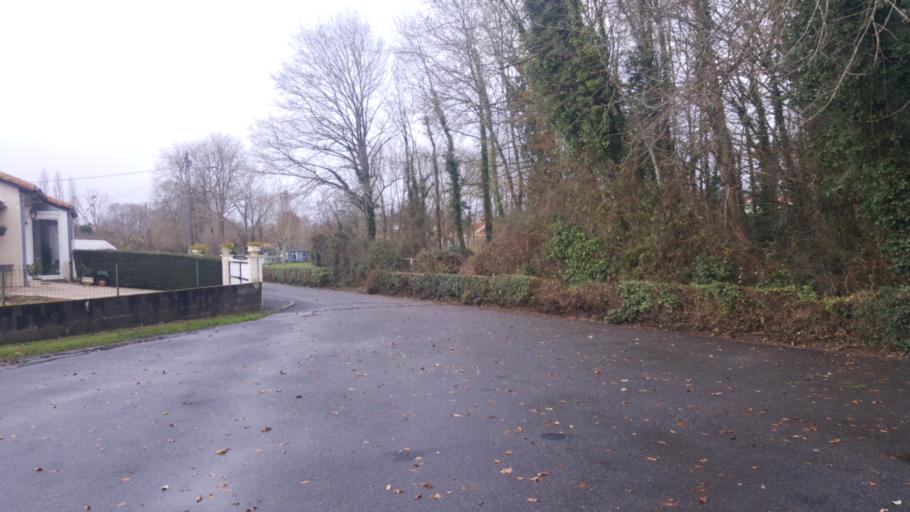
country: FR
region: Poitou-Charentes
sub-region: Departement des Deux-Sevres
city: Melle
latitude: 46.2260
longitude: -0.1345
